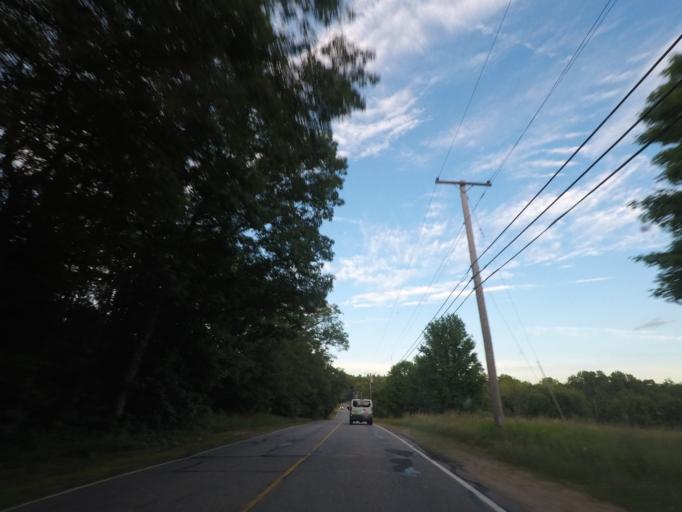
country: US
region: Massachusetts
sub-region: Worcester County
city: Warren
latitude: 42.1845
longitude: -72.1676
